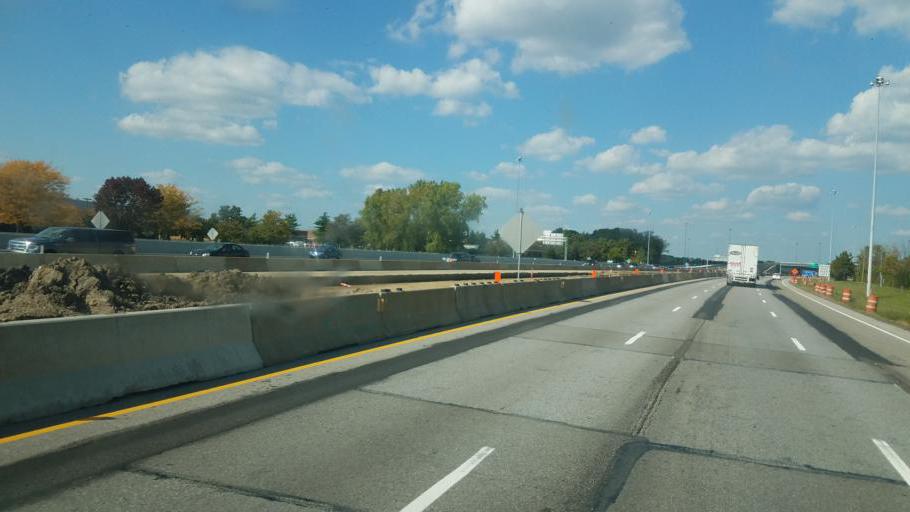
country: US
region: Ohio
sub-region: Franklin County
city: Dublin
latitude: 40.0917
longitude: -83.1379
